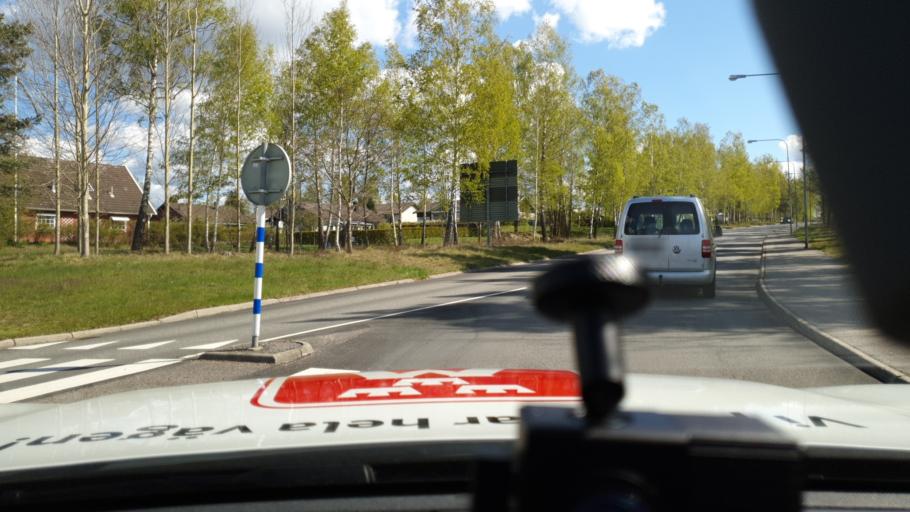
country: SE
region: Kalmar
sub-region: Vimmerby Kommun
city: Vimmerby
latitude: 57.6787
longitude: 15.8525
